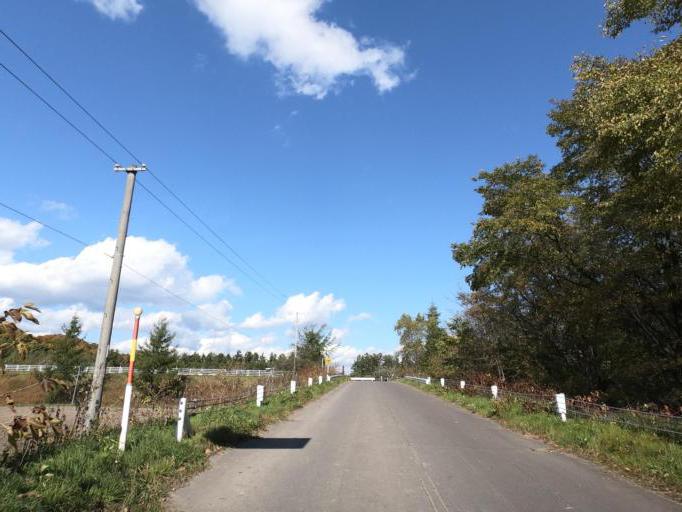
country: JP
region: Hokkaido
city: Otofuke
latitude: 43.2380
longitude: 143.2689
